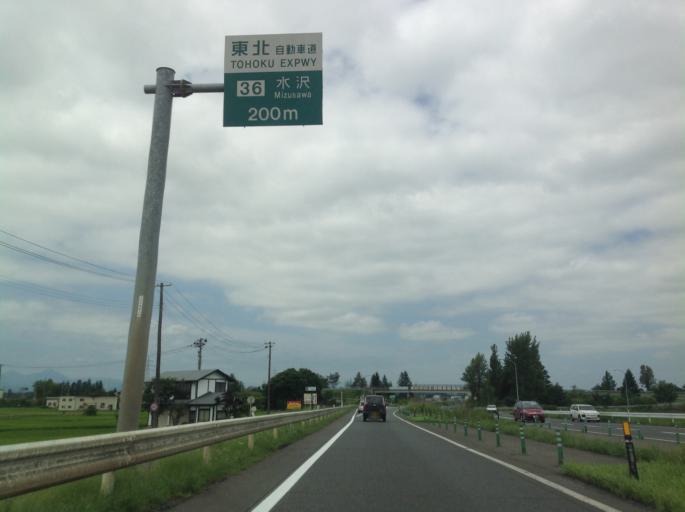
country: JP
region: Iwate
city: Mizusawa
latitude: 39.1706
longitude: 141.1253
